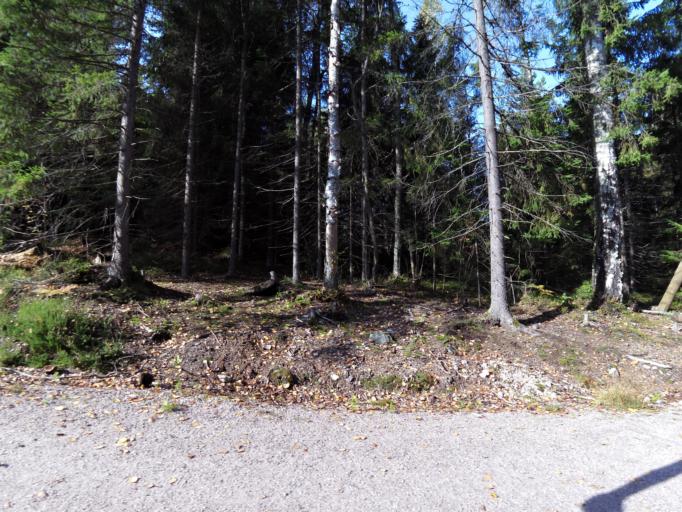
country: FI
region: Uusimaa
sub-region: Helsinki
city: Espoo
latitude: 60.1785
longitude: 24.6332
